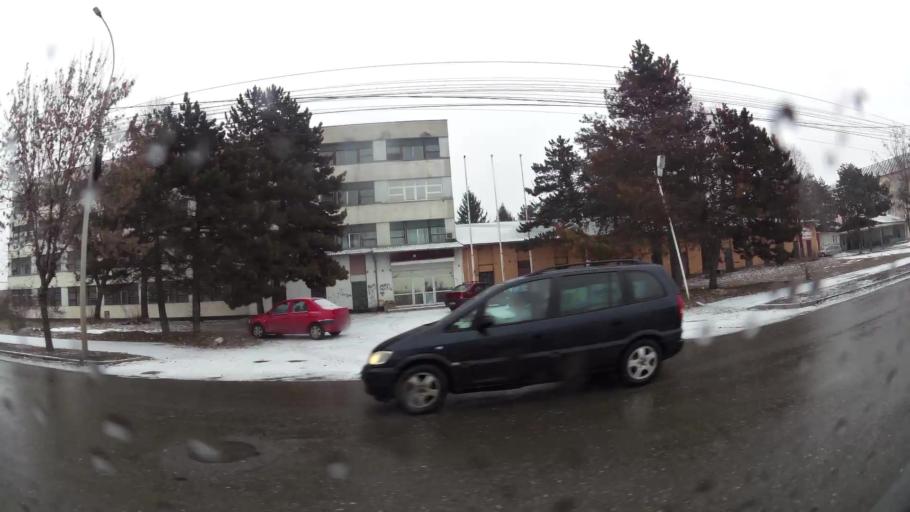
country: RO
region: Dambovita
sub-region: Municipiul Targoviste
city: Targoviste
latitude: 44.9164
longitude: 25.4401
